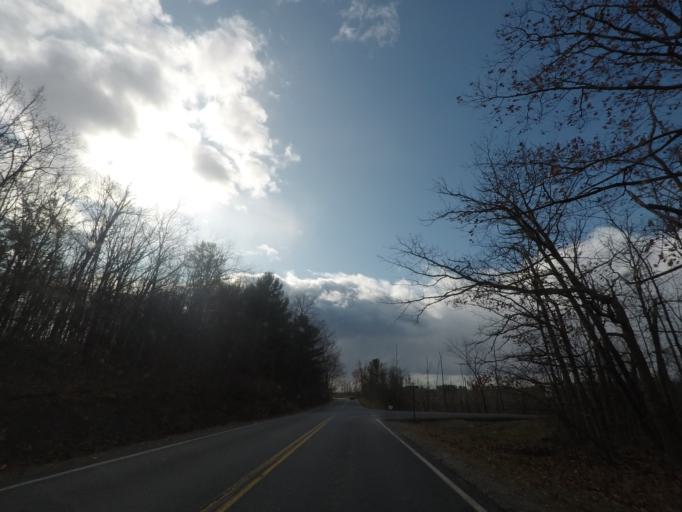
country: US
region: New York
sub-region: Saratoga County
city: Ballston Spa
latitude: 42.9566
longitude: -73.8461
